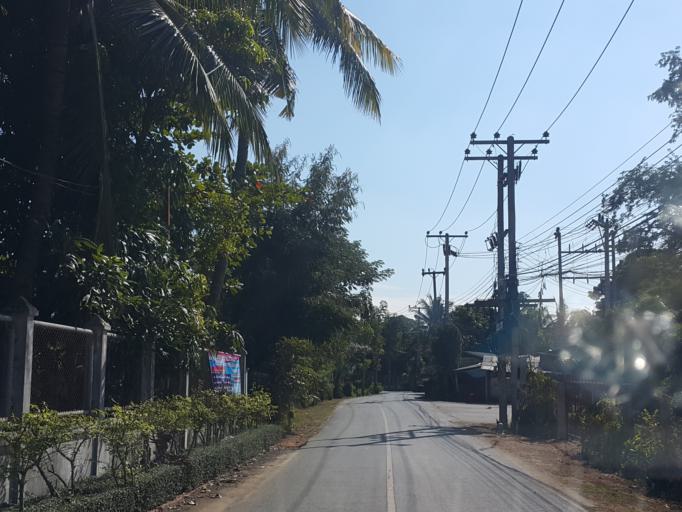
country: TH
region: Chiang Mai
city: San Sai
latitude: 18.8785
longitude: 99.0014
